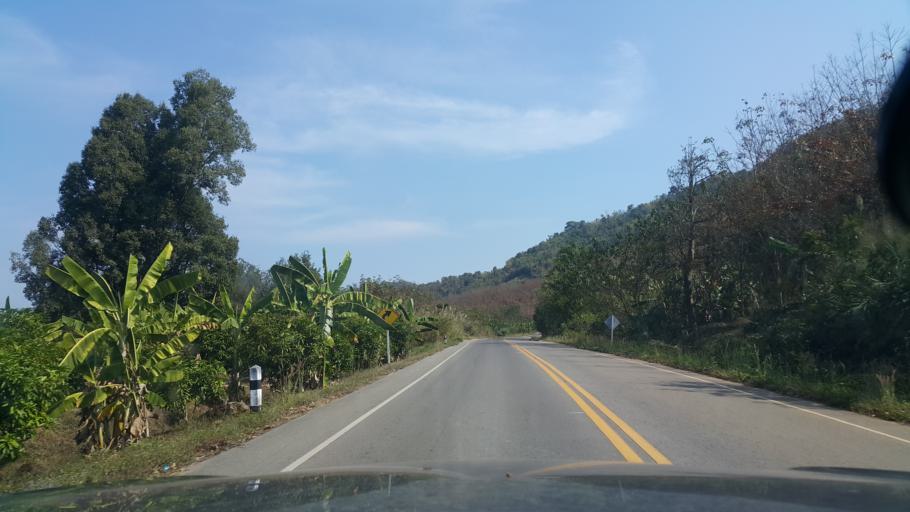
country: TH
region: Loei
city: Pak Chom
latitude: 18.1021
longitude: 102.0399
